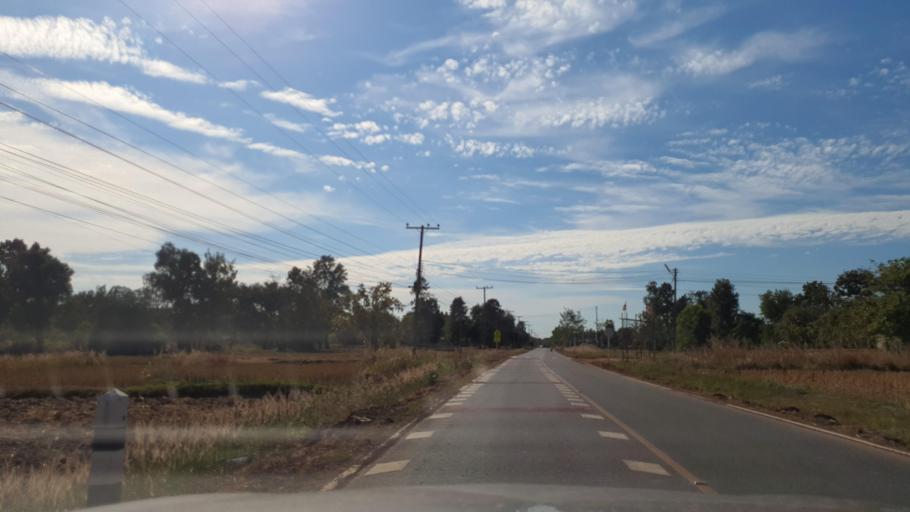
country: TH
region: Kalasin
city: Kuchinarai
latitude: 16.5431
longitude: 104.0915
